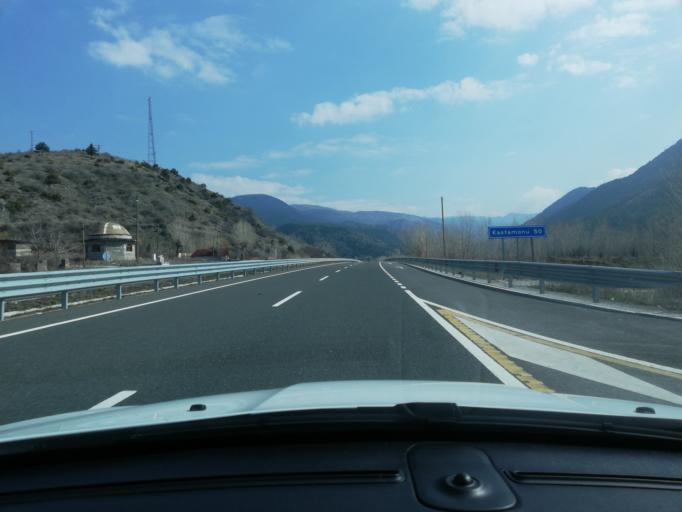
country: TR
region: Cankiri
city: Ilgaz
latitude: 40.9700
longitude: 33.6889
